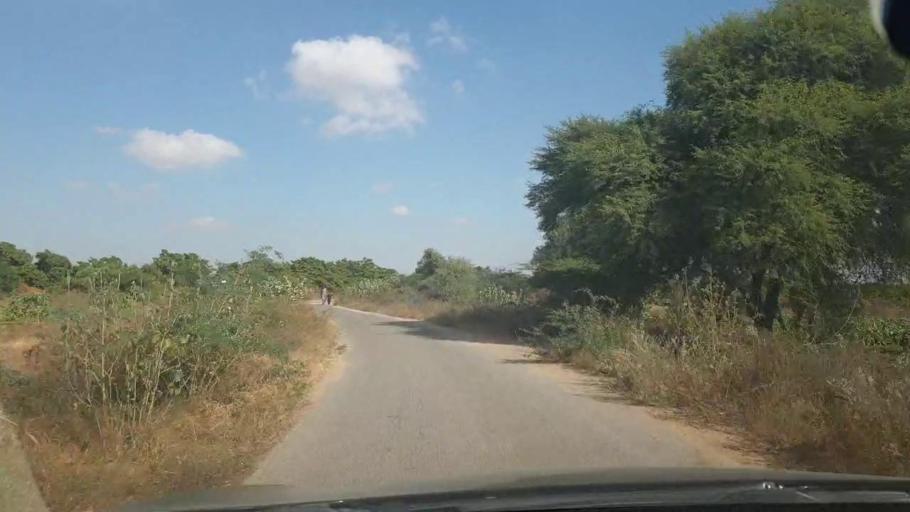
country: PK
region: Sindh
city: Malir Cantonment
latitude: 25.0557
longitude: 67.3900
